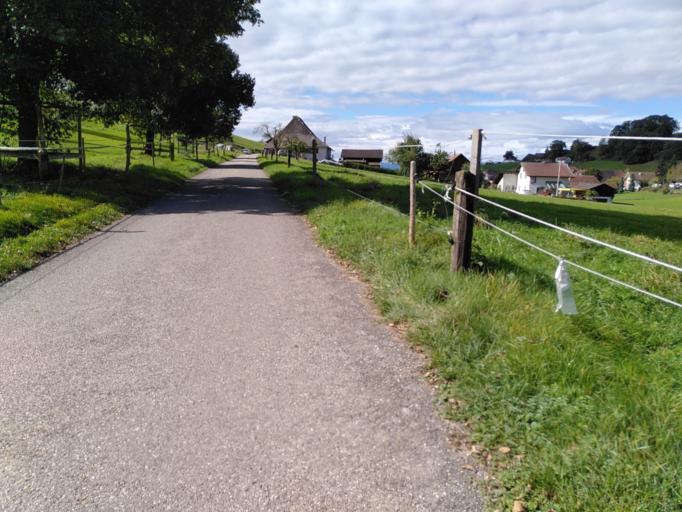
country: CH
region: Bern
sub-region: Emmental District
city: Wynigen
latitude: 47.1232
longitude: 7.6414
